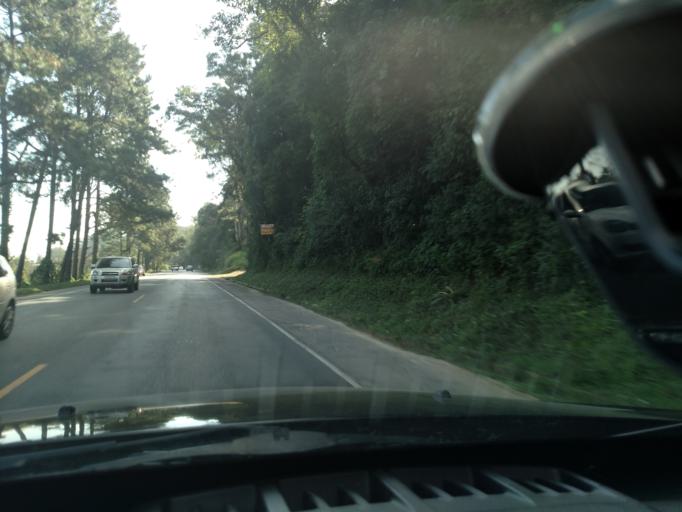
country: BR
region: Santa Catarina
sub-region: Rio Do Sul
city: Rio do Sul
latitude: -27.2346
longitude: -49.6764
